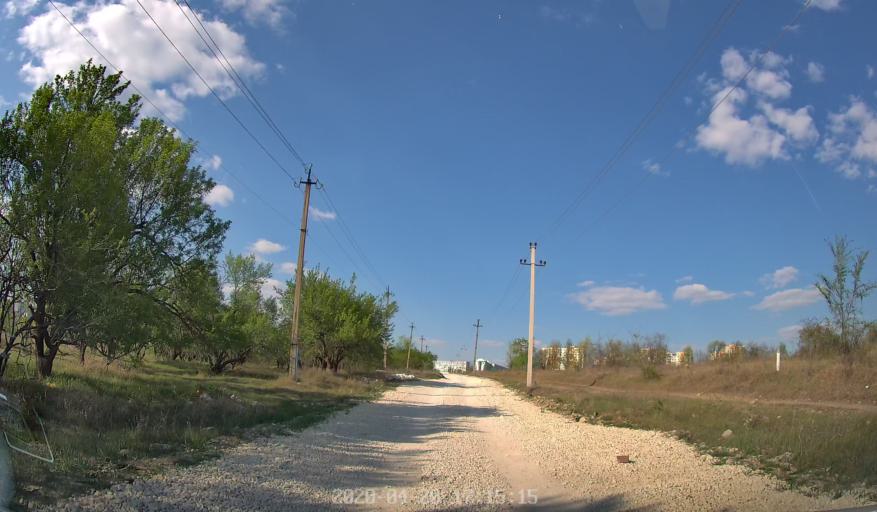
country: MD
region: Chisinau
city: Chisinau
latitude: 46.9693
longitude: 28.8444
